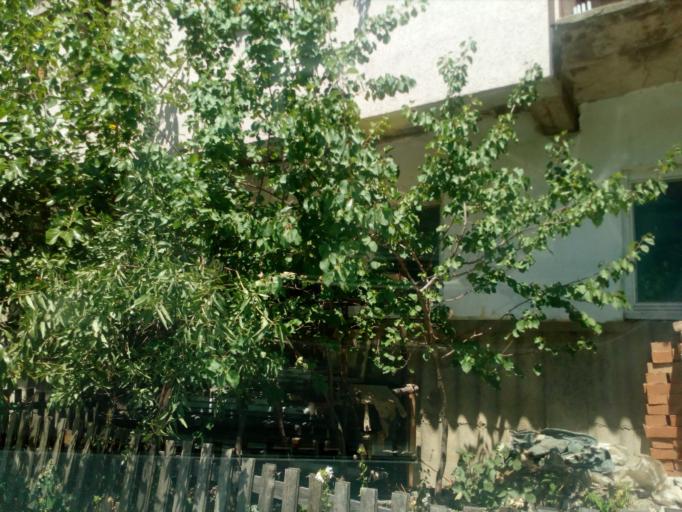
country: MK
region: Veles
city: Veles
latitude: 41.7128
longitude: 21.7888
